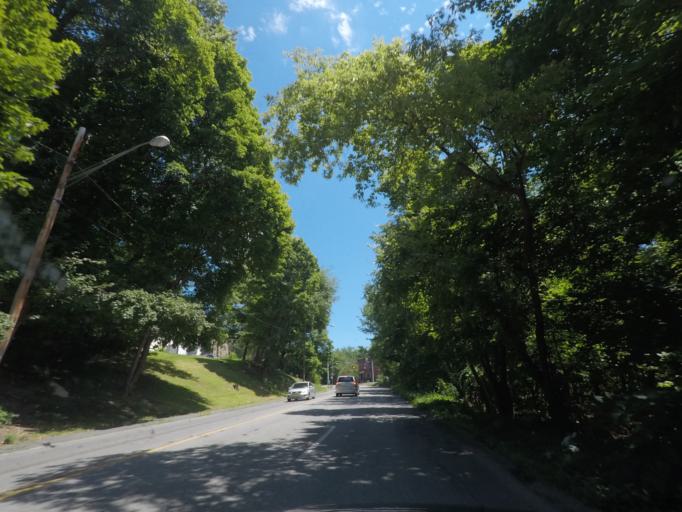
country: US
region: New York
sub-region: Rensselaer County
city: Troy
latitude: 42.7045
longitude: -73.6933
